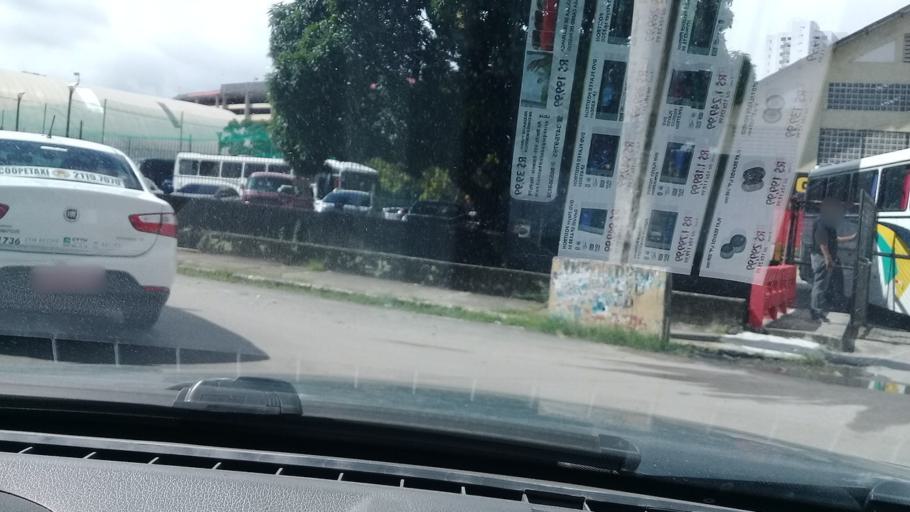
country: BR
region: Pernambuco
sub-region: Recife
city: Recife
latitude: -8.0646
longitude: -34.9045
